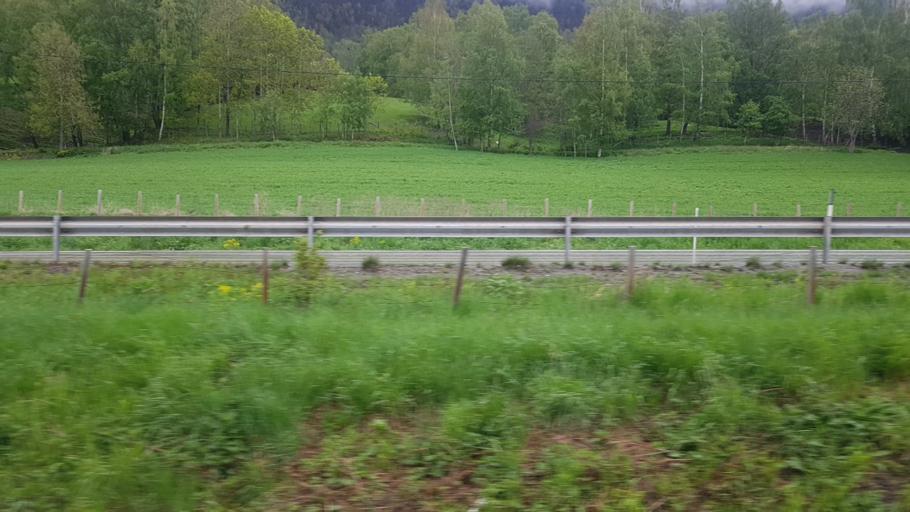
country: NO
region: Oppland
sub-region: Nord-Fron
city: Vinstra
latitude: 61.6205
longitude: 9.7147
